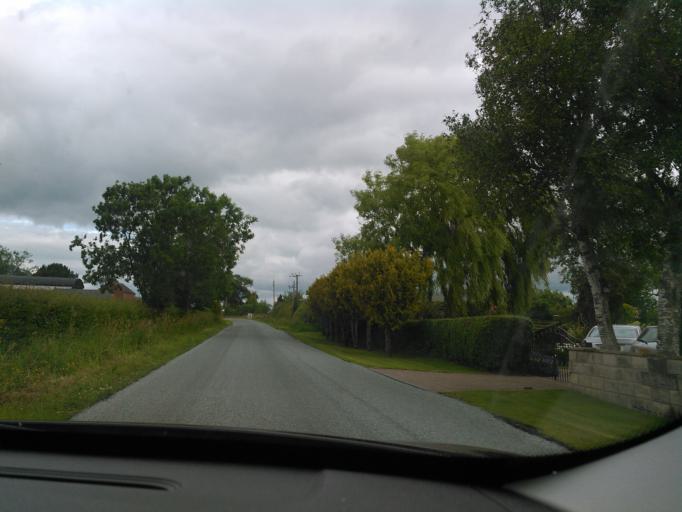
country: GB
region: England
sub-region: Shropshire
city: Wem
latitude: 52.8969
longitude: -2.7611
